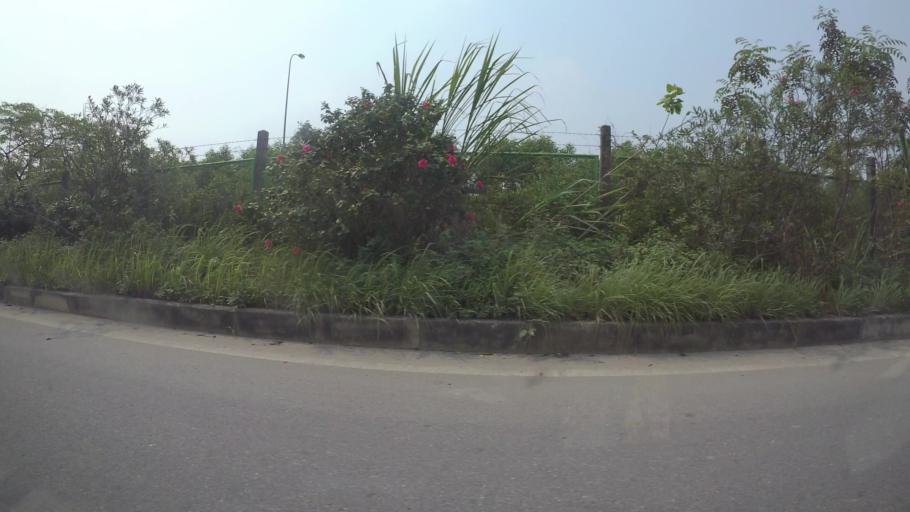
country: VN
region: Ha Noi
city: Quoc Oai
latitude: 21.0018
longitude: 105.6131
